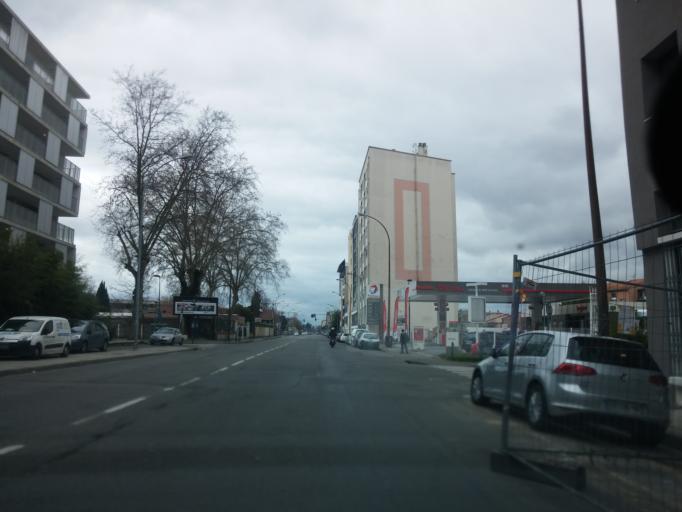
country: FR
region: Midi-Pyrenees
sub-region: Departement de la Haute-Garonne
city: Toulouse
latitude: 43.5988
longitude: 1.4179
